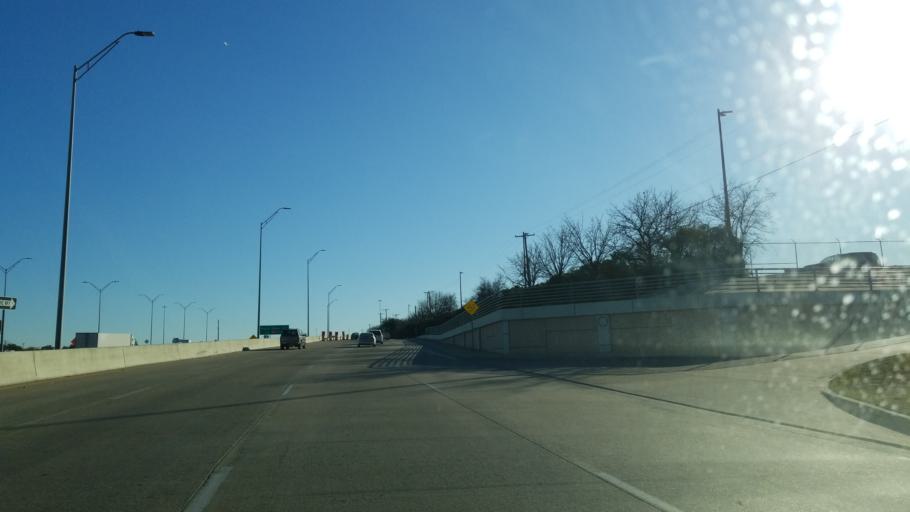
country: US
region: Texas
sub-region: Tarrant County
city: Arlington
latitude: 32.7421
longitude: -97.0630
